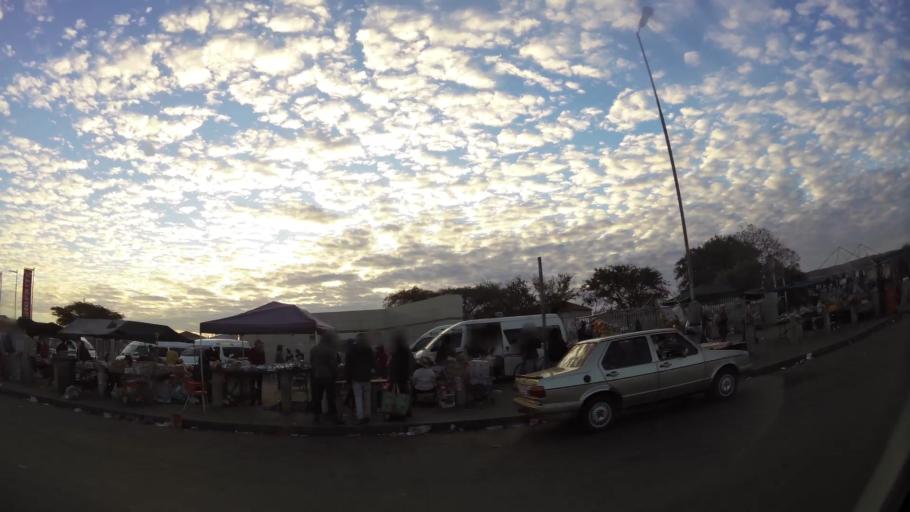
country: ZA
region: Gauteng
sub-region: City of Tshwane Metropolitan Municipality
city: Pretoria
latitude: -25.7149
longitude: 28.3350
